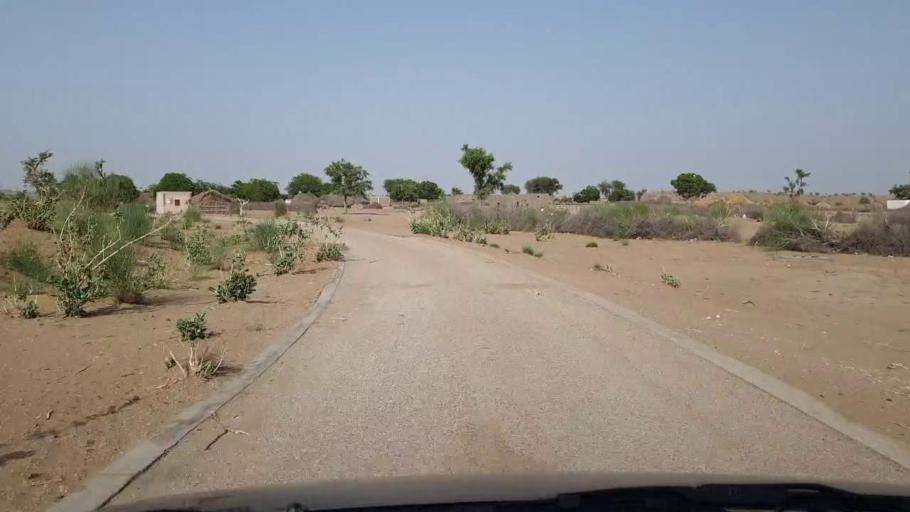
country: PK
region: Sindh
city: Chor
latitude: 25.4532
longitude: 70.5305
